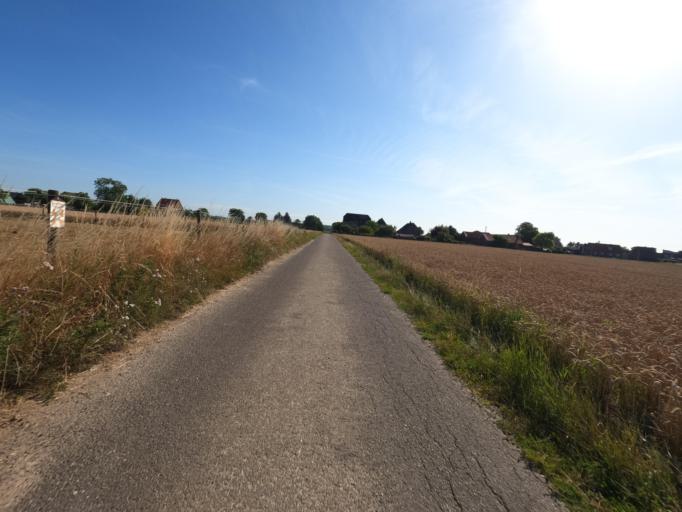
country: DE
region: North Rhine-Westphalia
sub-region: Regierungsbezirk Koln
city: Heinsberg
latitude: 51.0785
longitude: 6.1194
